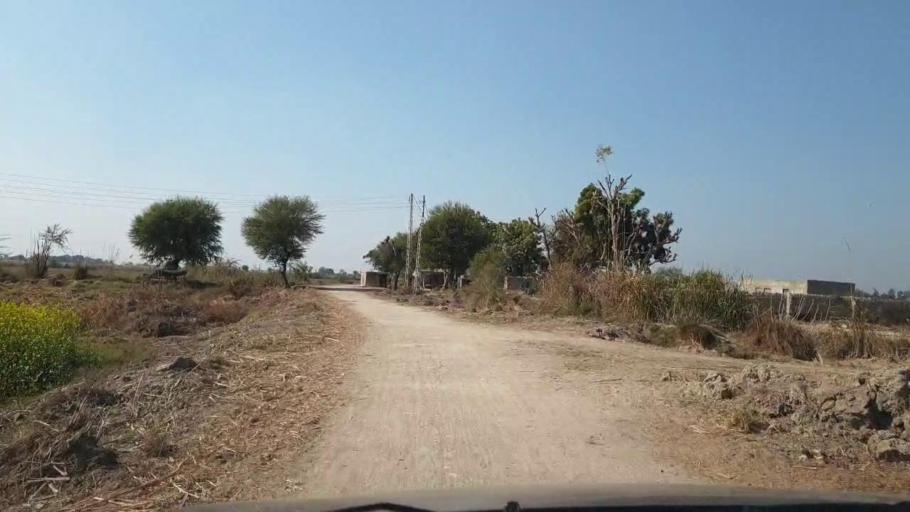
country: PK
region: Sindh
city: Jhol
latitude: 25.9127
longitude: 68.8159
